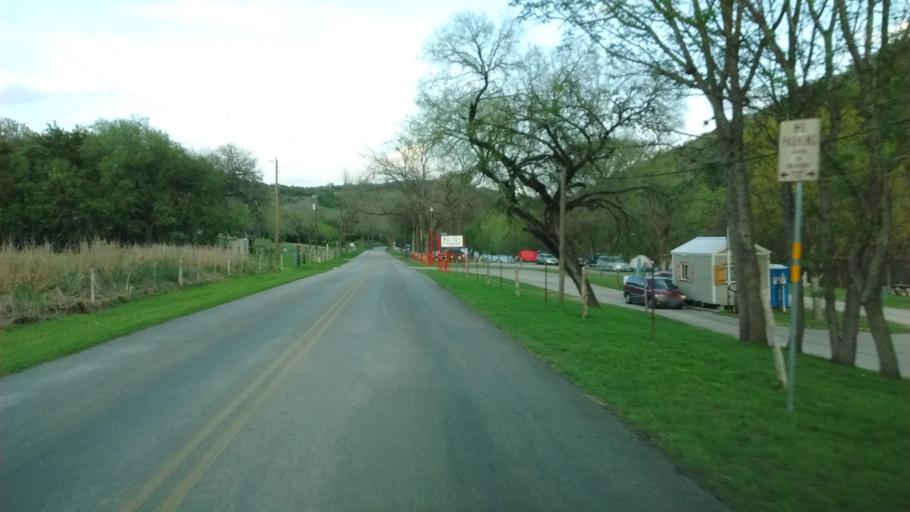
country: US
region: Texas
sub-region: Comal County
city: New Braunfels
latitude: 29.7650
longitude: -98.1532
